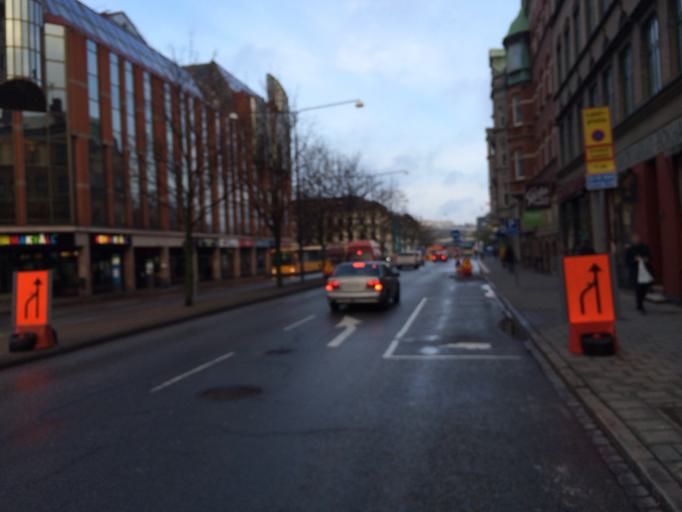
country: SE
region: Skane
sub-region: Malmo
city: Malmoe
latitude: 55.5997
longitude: 13.0081
